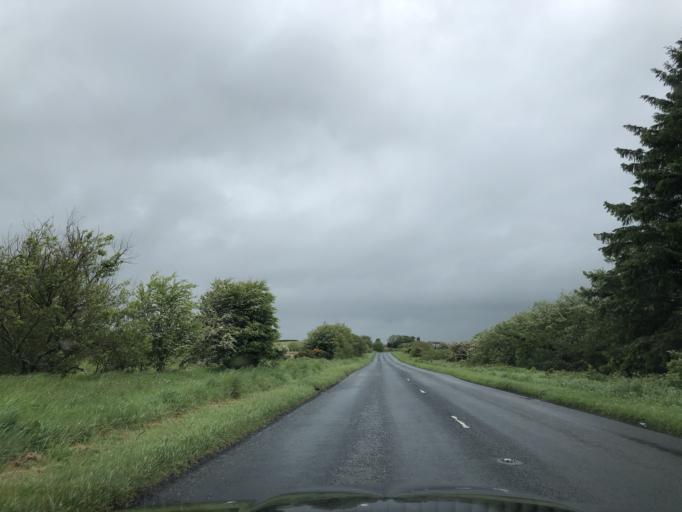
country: GB
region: Northern Ireland
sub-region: Moyle District
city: Ballycastle
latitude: 55.1660
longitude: -6.3615
